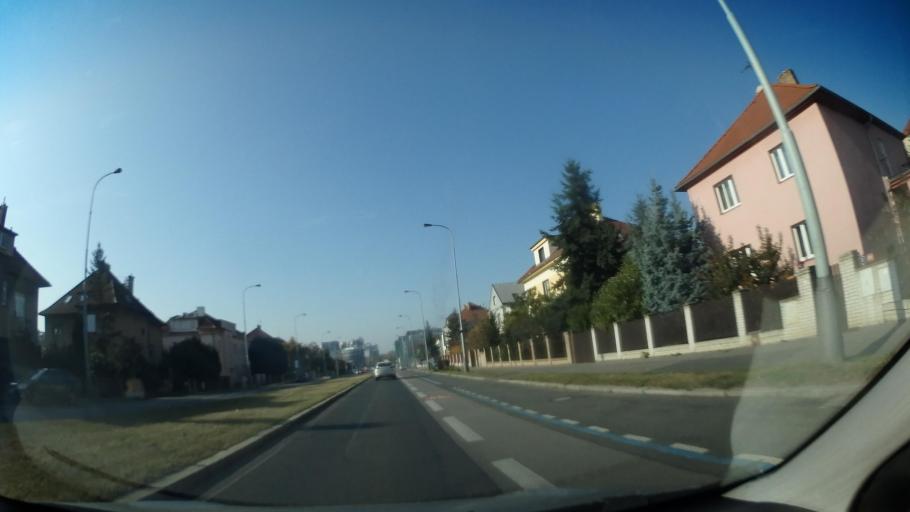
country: CZ
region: Praha
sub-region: Praha 8
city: Liben
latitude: 50.0807
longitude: 14.4914
